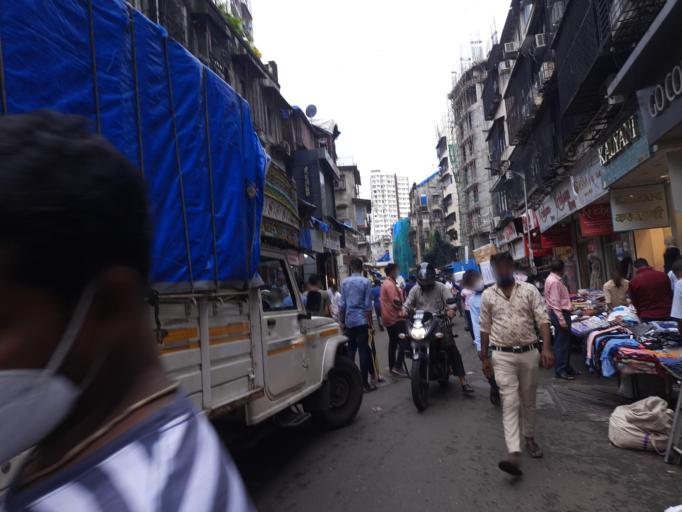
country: IN
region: Maharashtra
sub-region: Mumbai Suburban
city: Mumbai
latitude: 18.9526
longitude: 72.8275
